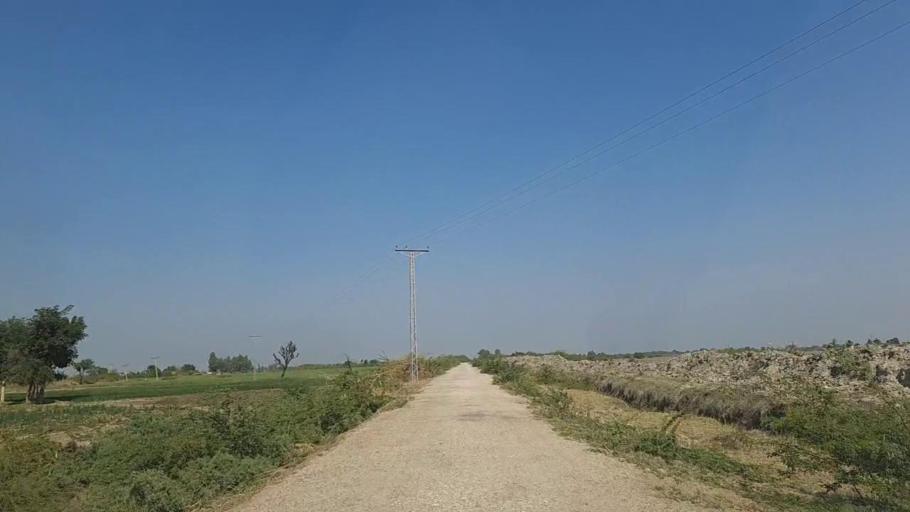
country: PK
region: Sindh
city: Digri
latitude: 25.1866
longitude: 69.1446
